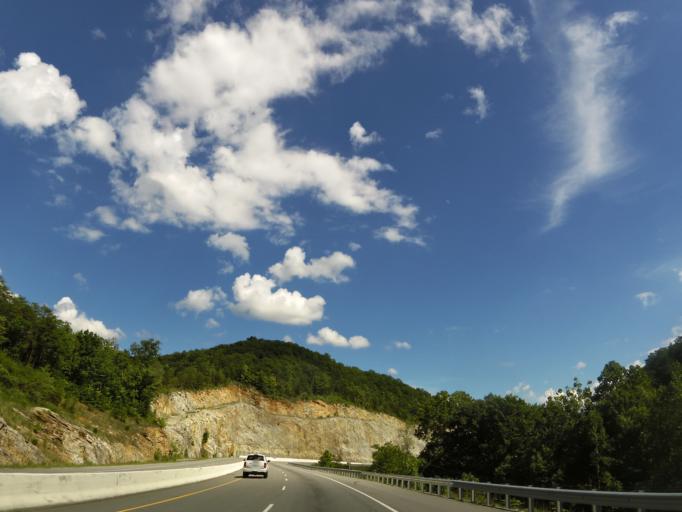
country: US
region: Tennessee
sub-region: Claiborne County
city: Tazewell
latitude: 36.3965
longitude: -83.4541
